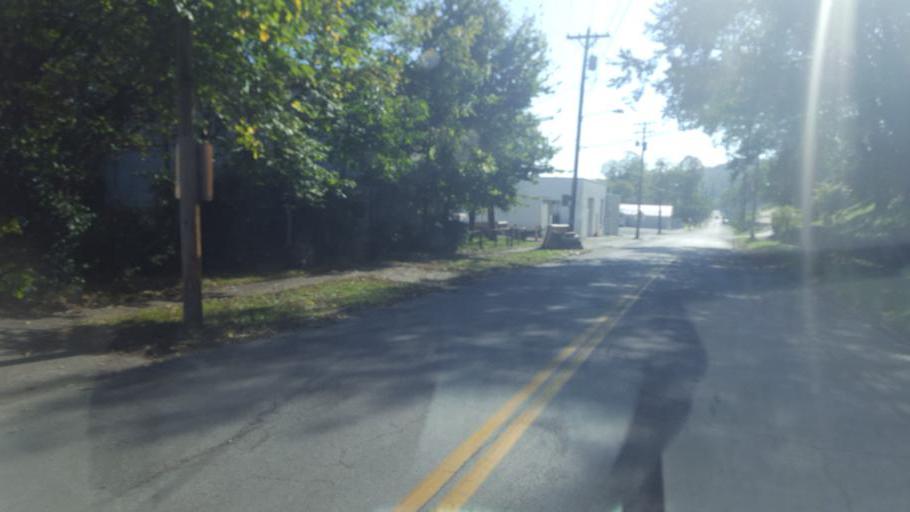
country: US
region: Ohio
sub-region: Brown County
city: Aberdeen
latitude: 38.6446
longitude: -83.7630
